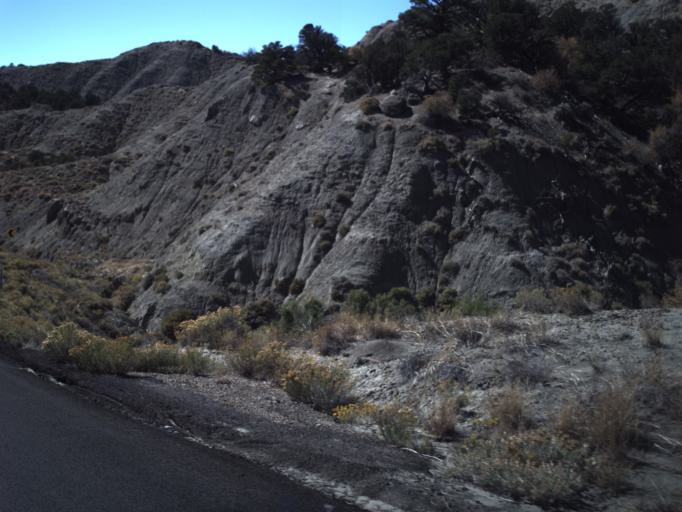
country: US
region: Utah
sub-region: Garfield County
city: Panguitch
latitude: 37.6315
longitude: -111.8461
